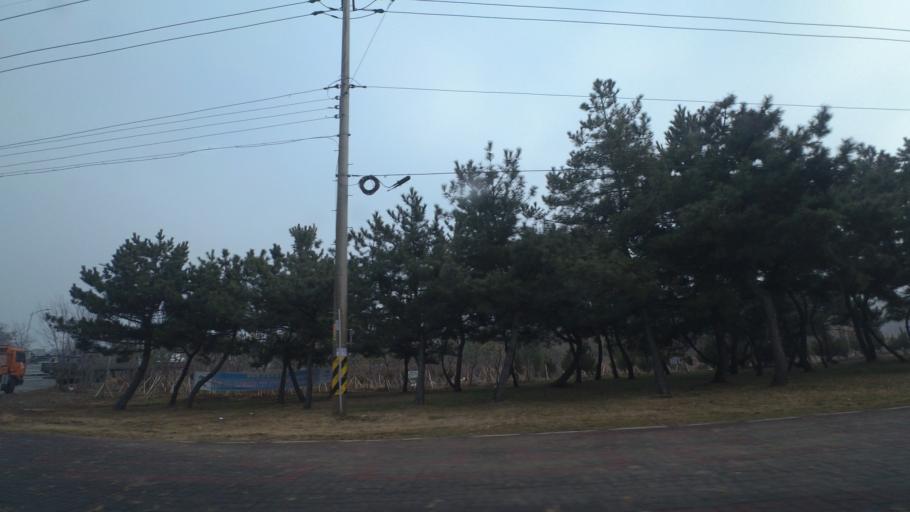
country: KR
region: Gyeonggi-do
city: Hwaseong-si
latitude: 36.9914
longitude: 126.8512
